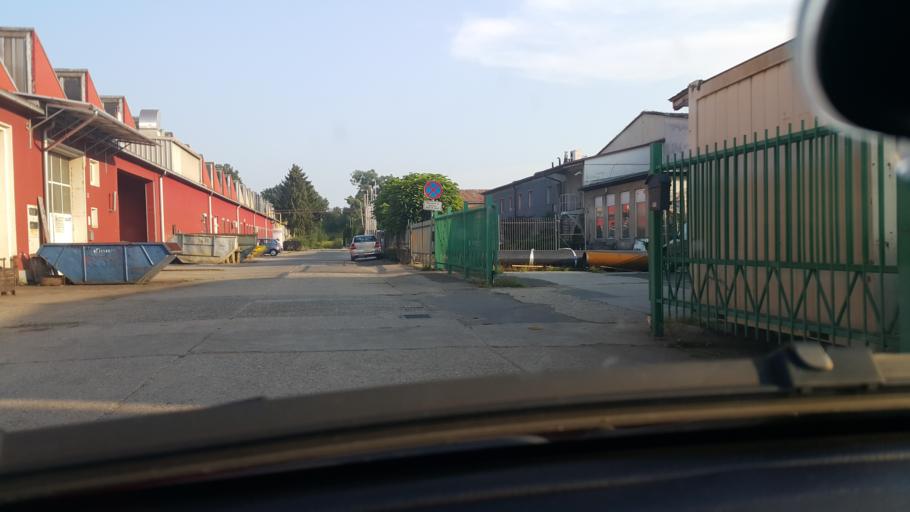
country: SI
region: Maribor
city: Razvanje
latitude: 46.5258
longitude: 15.6603
